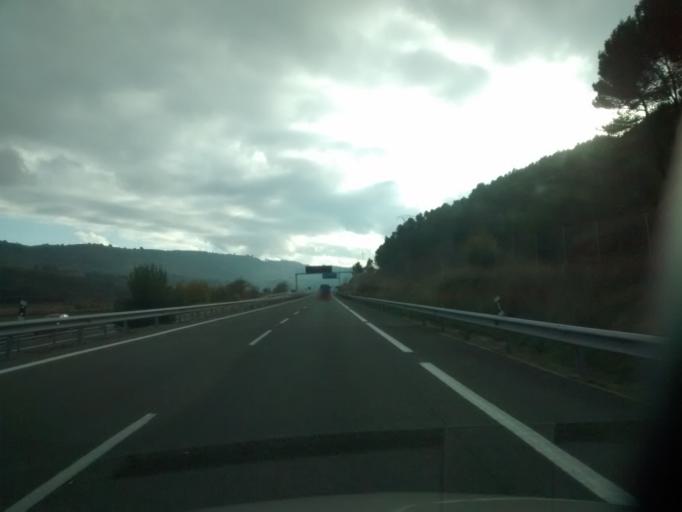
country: ES
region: Castille-La Mancha
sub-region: Provincia de Guadalajara
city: Tortola de Henares
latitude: 40.6967
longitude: -3.0844
